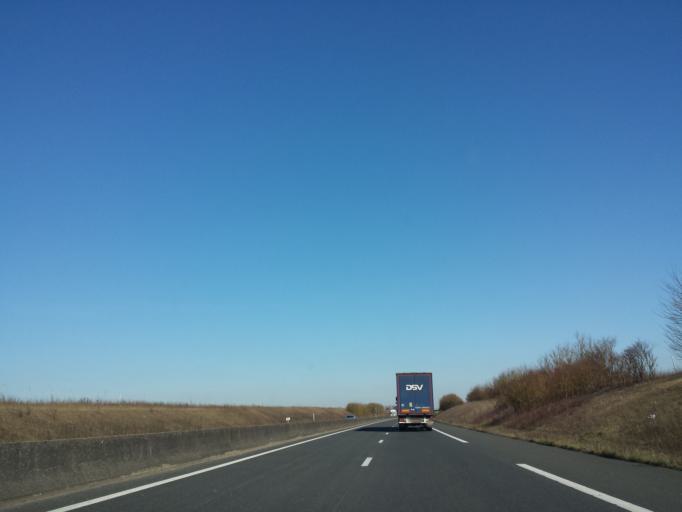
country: FR
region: Picardie
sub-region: Departement de l'Oise
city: Tille
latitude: 49.4861
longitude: 2.1656
